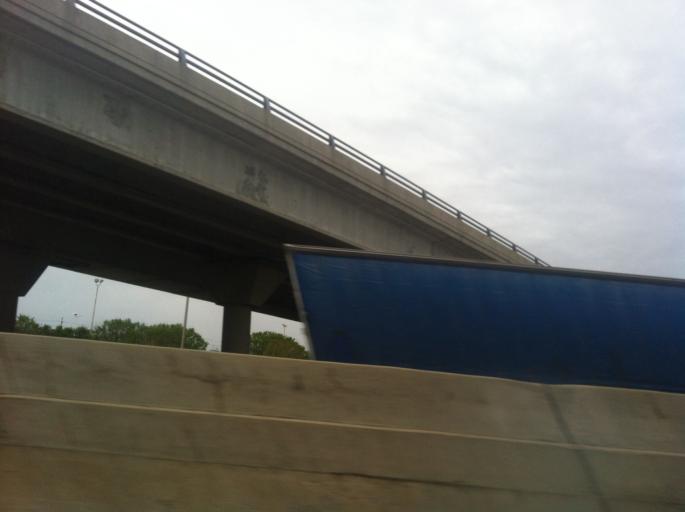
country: US
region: Illinois
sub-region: DuPage County
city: Downers Grove
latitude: 41.8097
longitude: -88.0371
